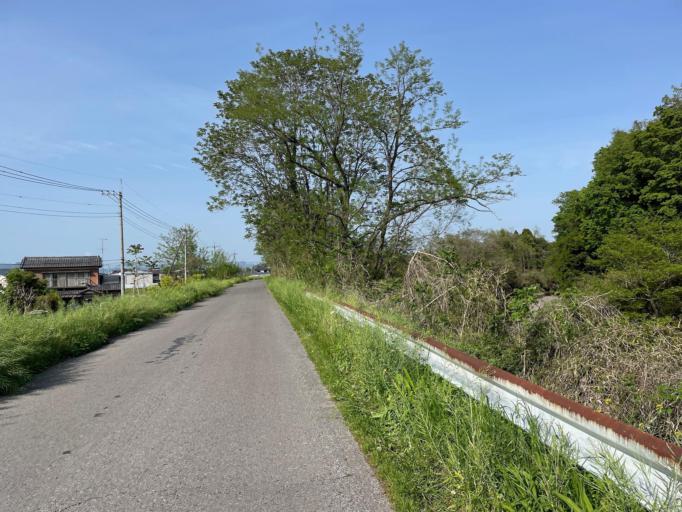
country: JP
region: Tochigi
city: Sano
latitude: 36.3109
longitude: 139.5363
